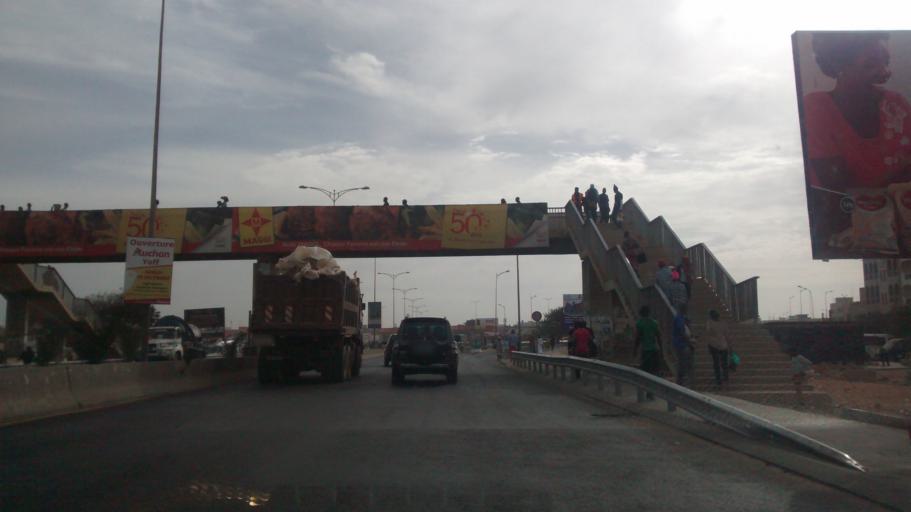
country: SN
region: Dakar
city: Grand Dakar
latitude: 14.7444
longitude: -17.4513
